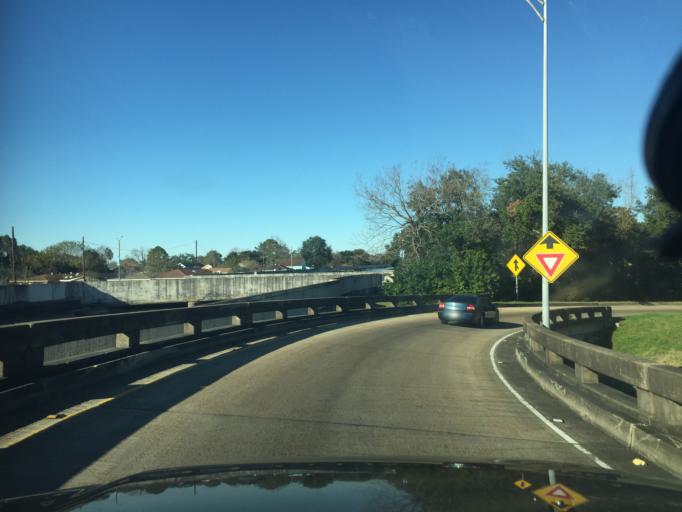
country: US
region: Louisiana
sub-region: Orleans Parish
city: New Orleans
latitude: 29.9914
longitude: -90.0678
